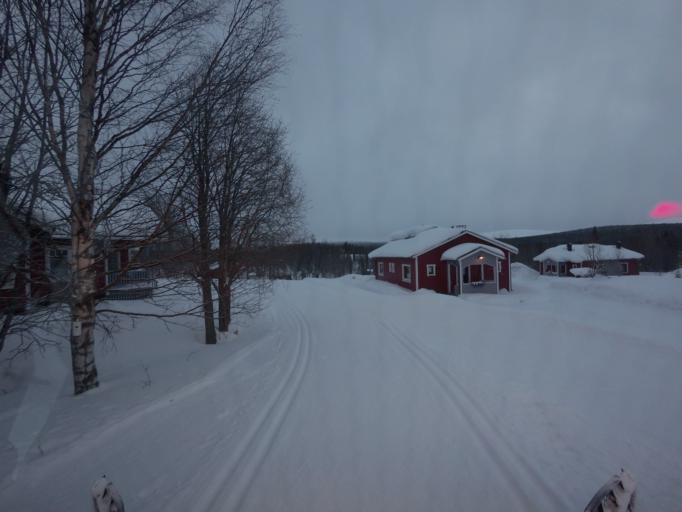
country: FI
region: Lapland
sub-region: Tunturi-Lappi
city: Kolari
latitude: 67.6137
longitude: 24.1546
